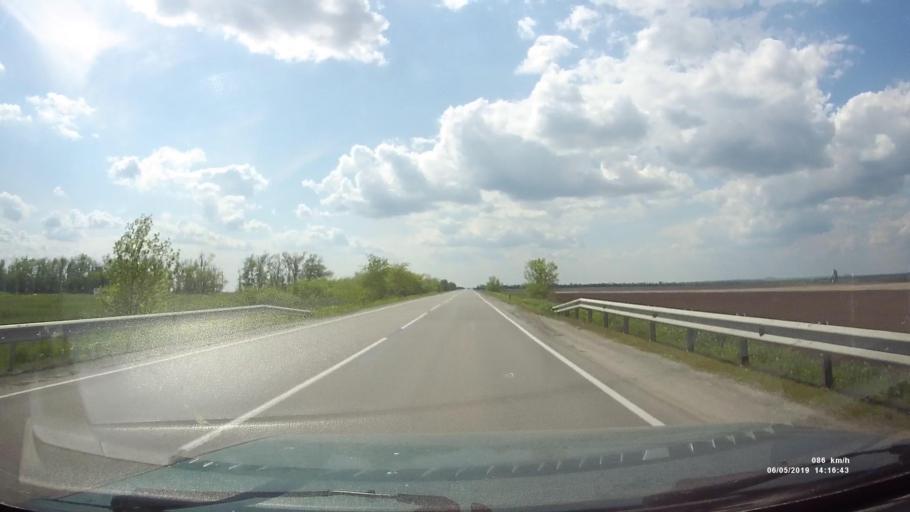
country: RU
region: Rostov
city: Kamenolomni
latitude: 47.6351
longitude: 40.2829
